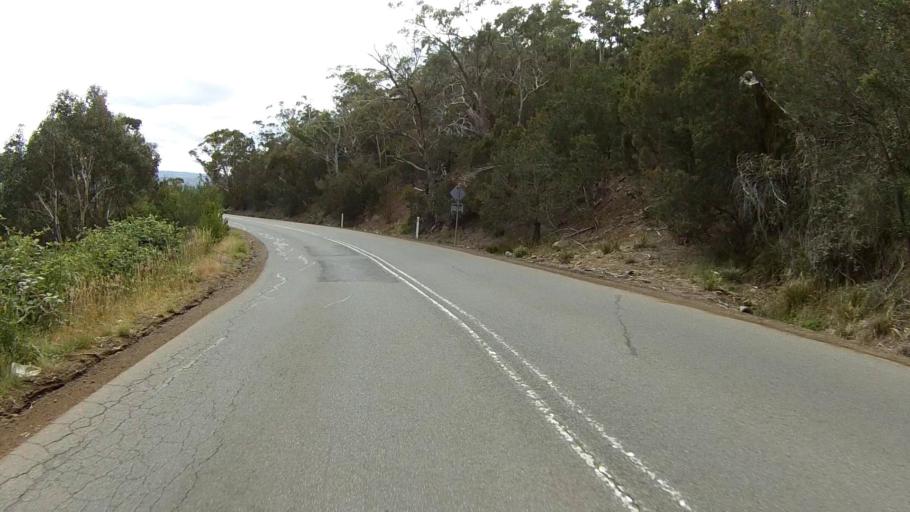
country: AU
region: Tasmania
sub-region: Clarence
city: Lindisfarne
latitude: -42.7801
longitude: 147.3657
